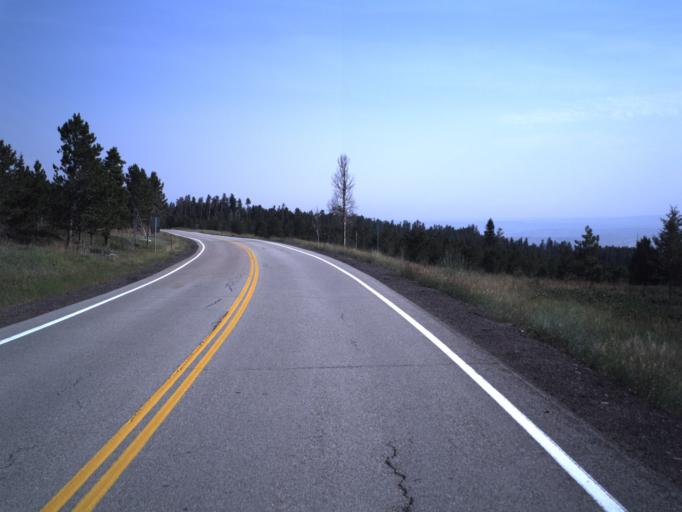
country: US
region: Utah
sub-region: Daggett County
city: Manila
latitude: 40.8402
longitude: -109.4644
